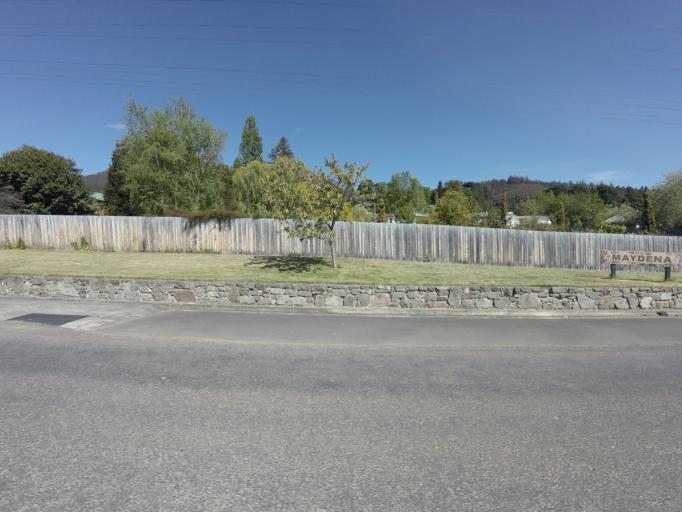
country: AU
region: Tasmania
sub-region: Derwent Valley
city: New Norfolk
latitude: -42.7555
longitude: 146.6256
